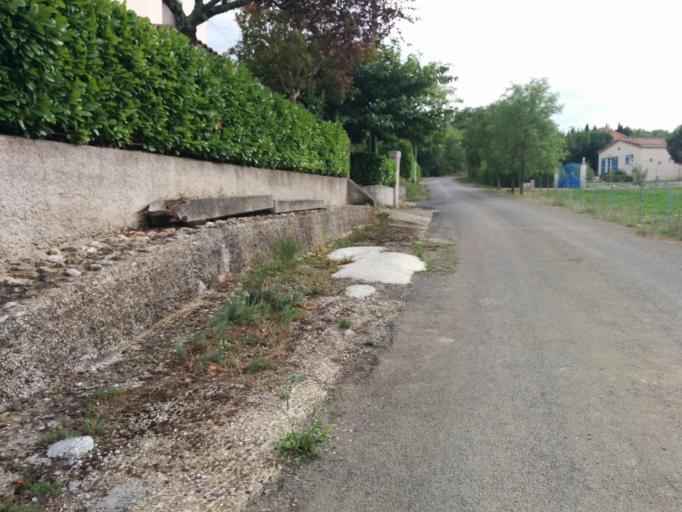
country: FR
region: Languedoc-Roussillon
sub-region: Departement du Gard
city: Saint-Christol-les-Ales
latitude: 44.0900
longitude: 4.0741
